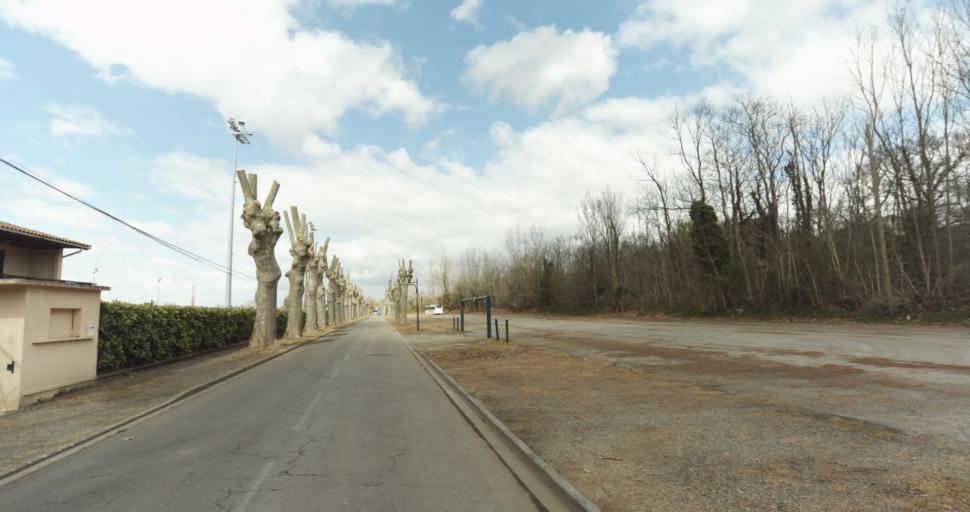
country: FR
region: Midi-Pyrenees
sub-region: Departement de la Haute-Garonne
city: Auterive
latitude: 43.3431
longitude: 1.4805
